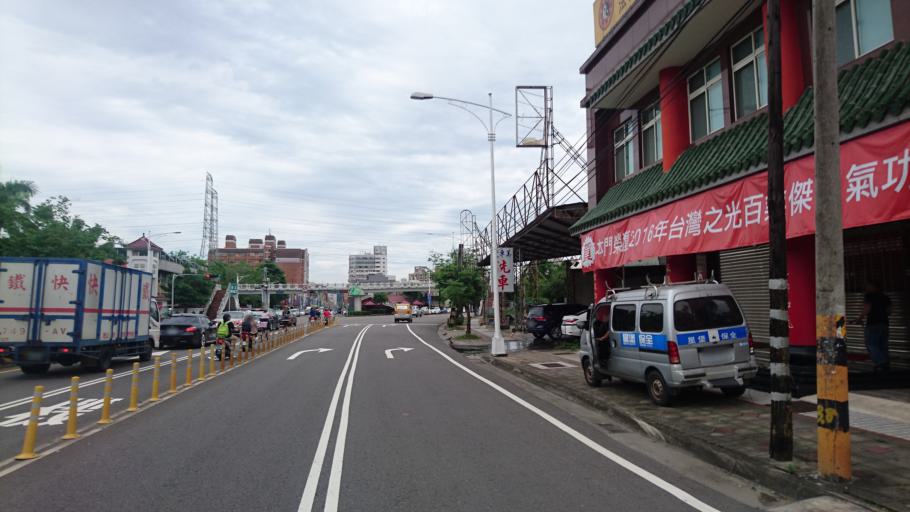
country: TW
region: Taiwan
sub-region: Taichung City
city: Taichung
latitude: 24.0744
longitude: 120.6998
